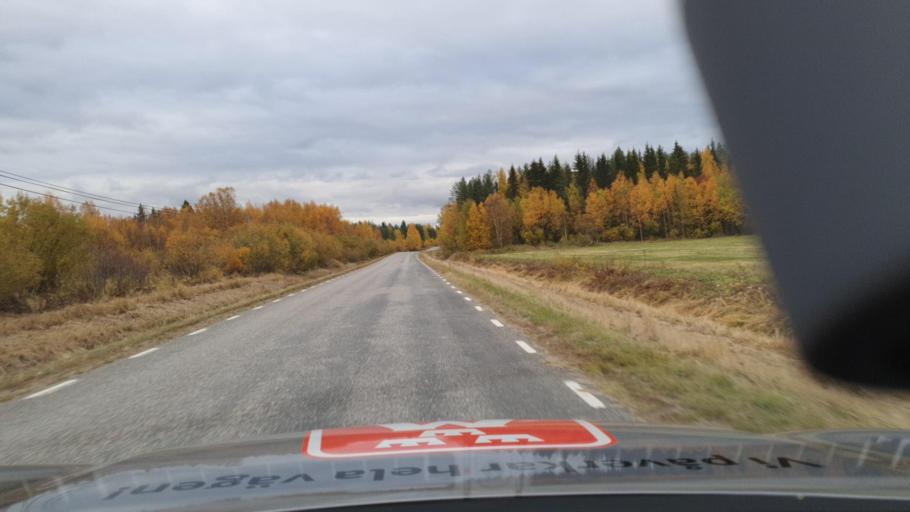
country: FI
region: Lapland
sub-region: Kemi-Tornio
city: Tornio
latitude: 66.0445
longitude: 23.9265
